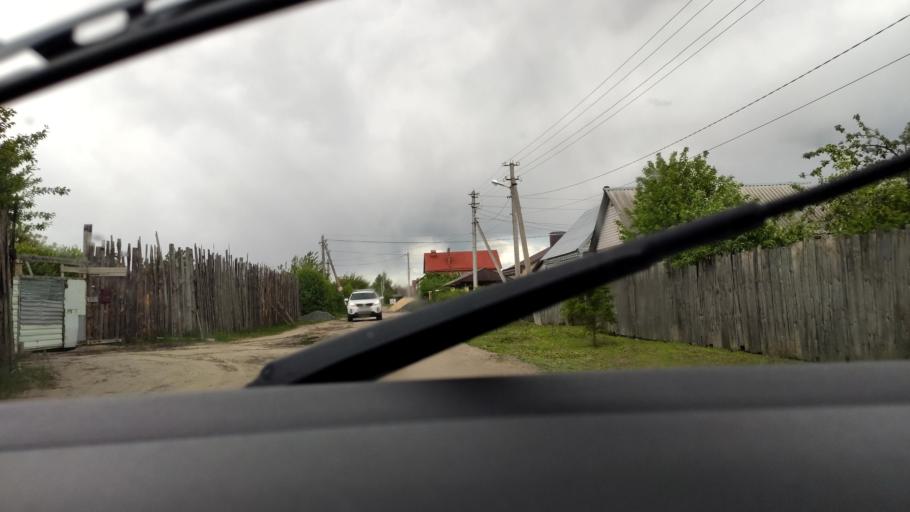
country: RU
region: Voronezj
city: Somovo
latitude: 51.6830
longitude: 39.3107
